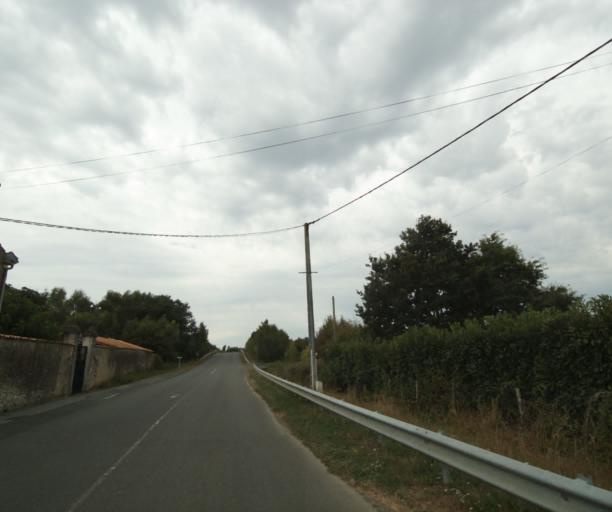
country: FR
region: Poitou-Charentes
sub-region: Departement de la Charente-Maritime
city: Tonnay-Charente
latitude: 45.9611
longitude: -0.8730
